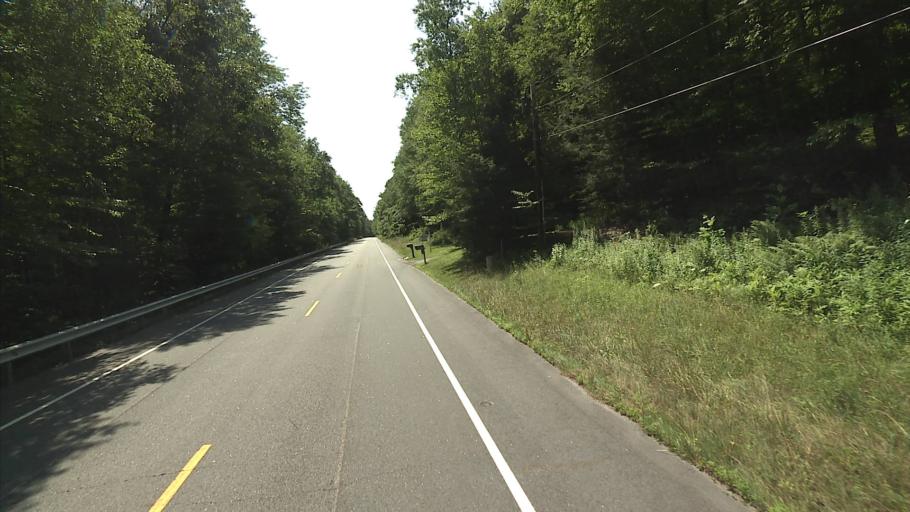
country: US
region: Connecticut
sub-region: Litchfield County
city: Winchester Center
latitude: 41.8873
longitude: -73.1740
